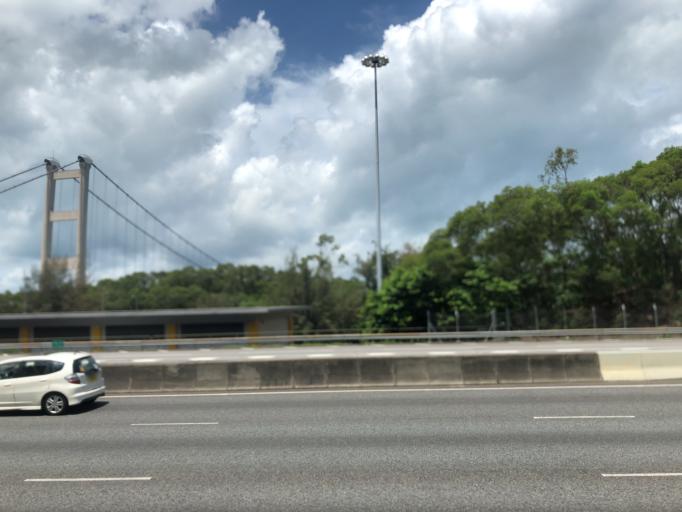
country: HK
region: Tsuen Wan
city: Tsuen Wan
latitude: 22.3576
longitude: 114.0833
